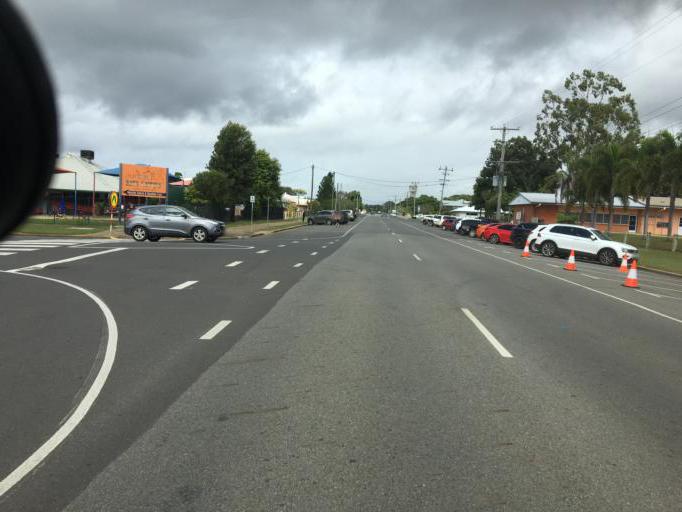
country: AU
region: Queensland
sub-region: Tablelands
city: Mareeba
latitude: -16.9958
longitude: 145.4254
